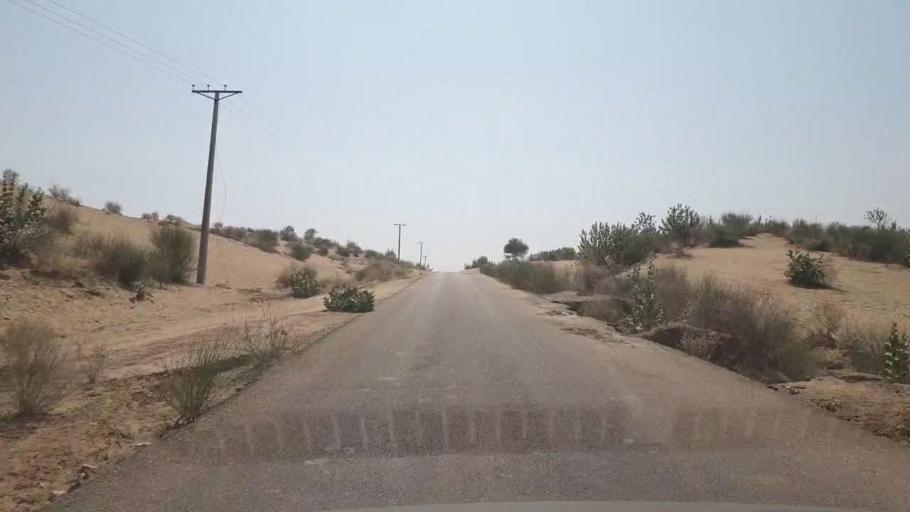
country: PK
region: Sindh
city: Chor
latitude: 25.6322
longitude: 70.1736
